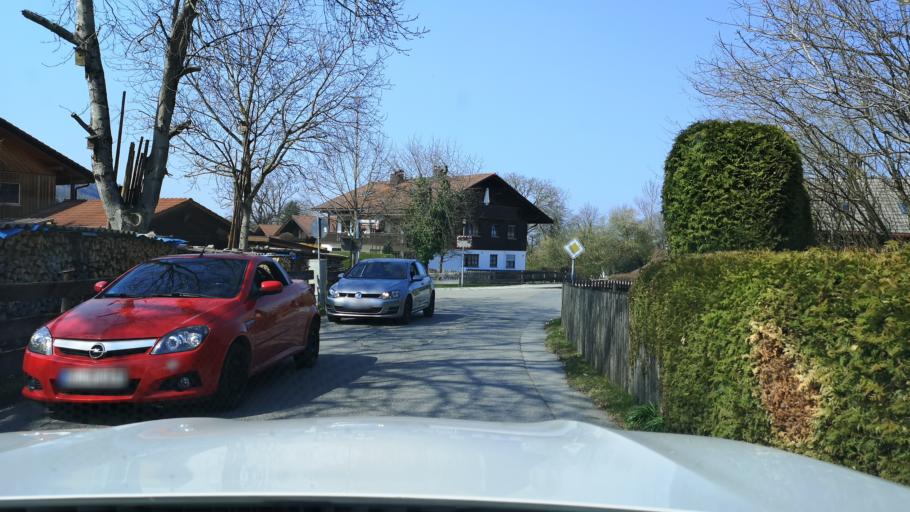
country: DE
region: Bavaria
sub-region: Upper Bavaria
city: Bad Feilnbach
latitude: 47.7686
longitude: 12.0129
